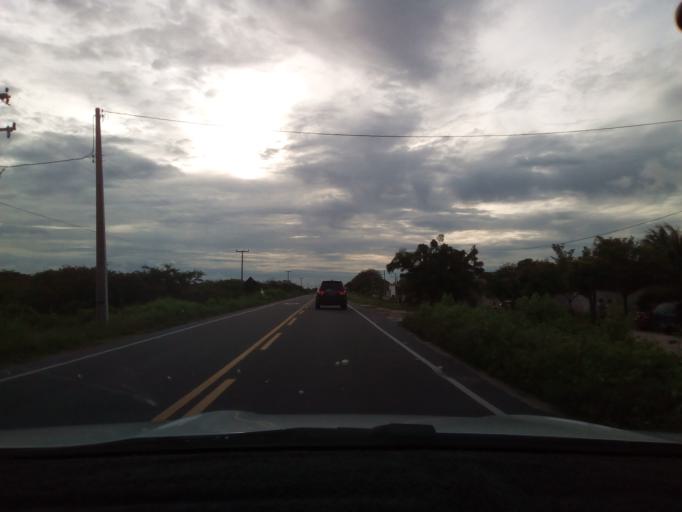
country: BR
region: Ceara
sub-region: Aracati
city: Aracati
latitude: -4.3939
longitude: -37.8678
